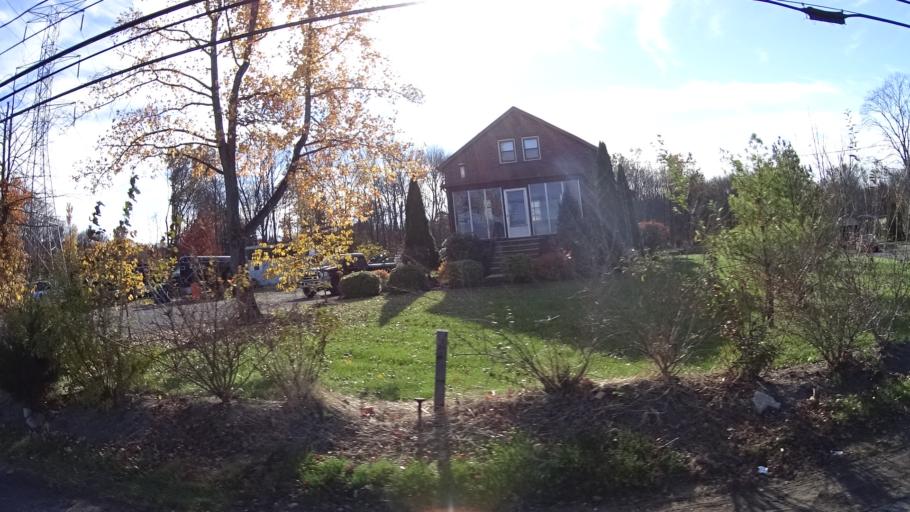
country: US
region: New Jersey
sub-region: Union County
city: Berkeley Heights
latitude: 40.6684
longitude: -74.4616
